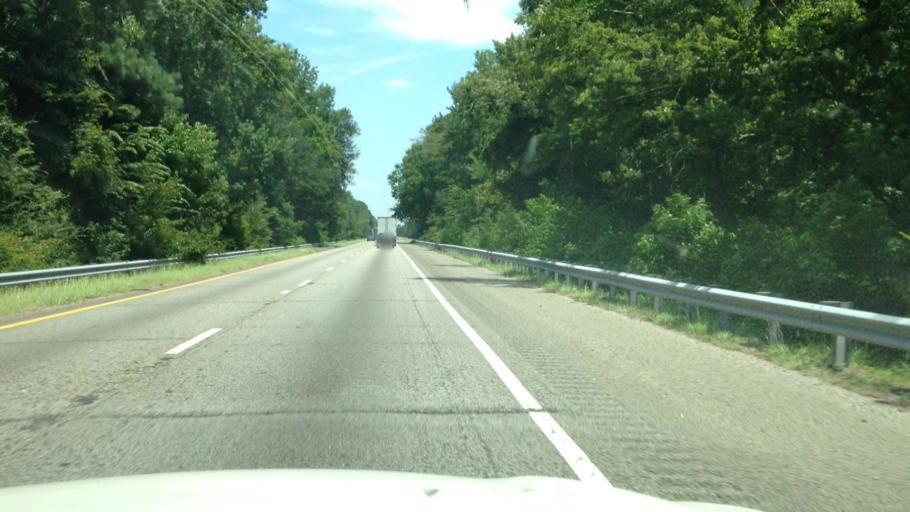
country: US
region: South Carolina
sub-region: Dillon County
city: Latta
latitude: 34.3131
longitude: -79.6057
